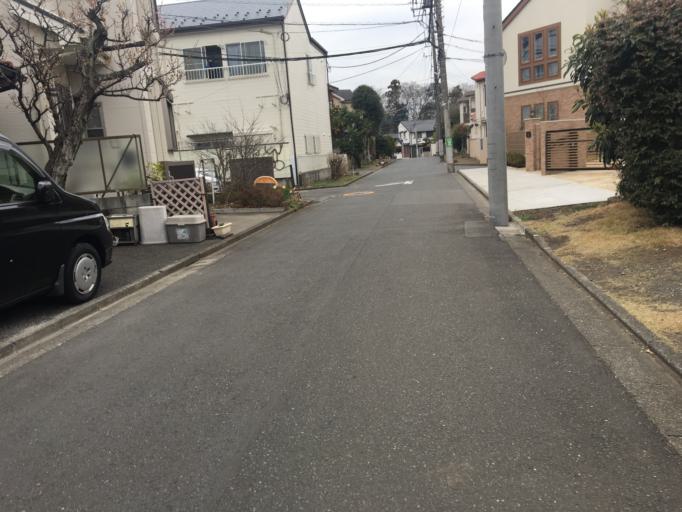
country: JP
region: Tokyo
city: Musashino
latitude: 35.6978
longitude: 139.5762
